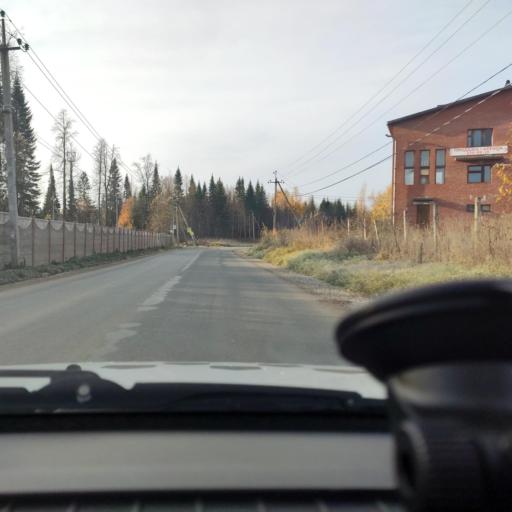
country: RU
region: Perm
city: Ferma
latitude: 57.9410
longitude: 56.4211
